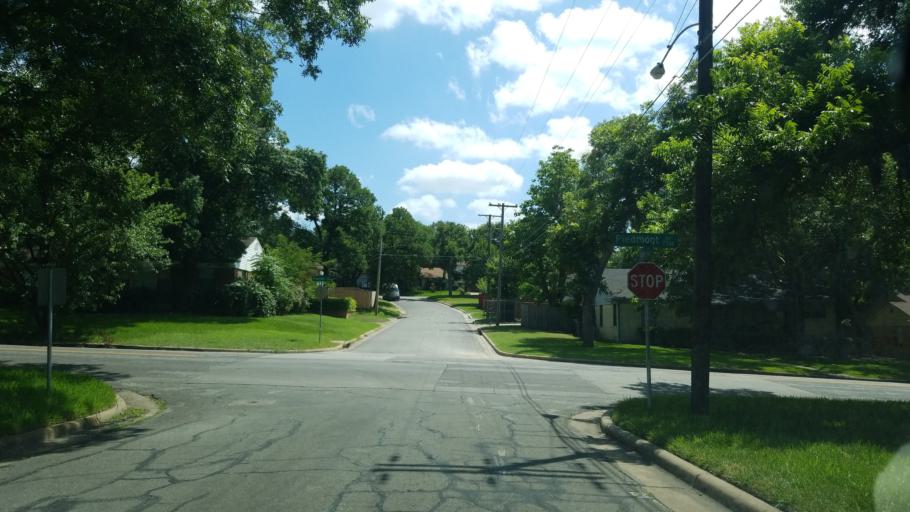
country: US
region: Texas
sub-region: Dallas County
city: Balch Springs
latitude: 32.7594
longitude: -96.6963
